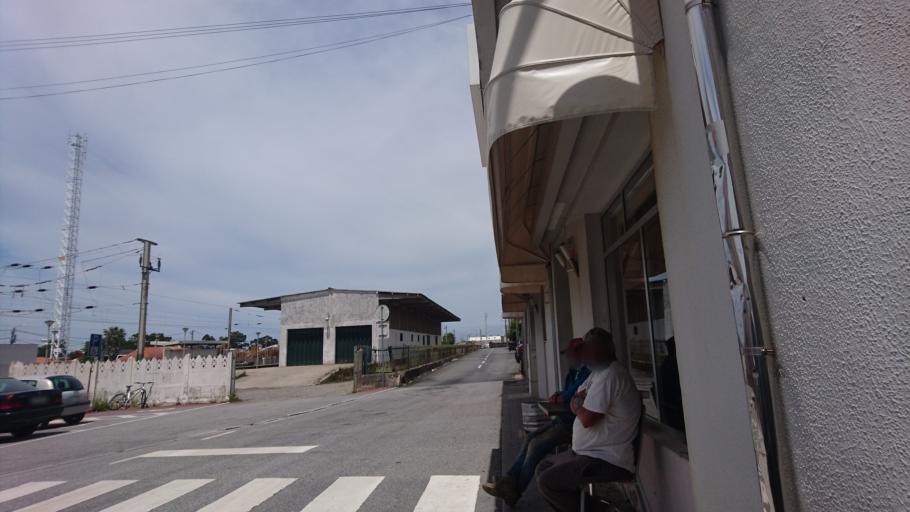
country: PT
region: Aveiro
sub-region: Ovar
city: Esmoriz
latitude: 40.9627
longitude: -8.6351
